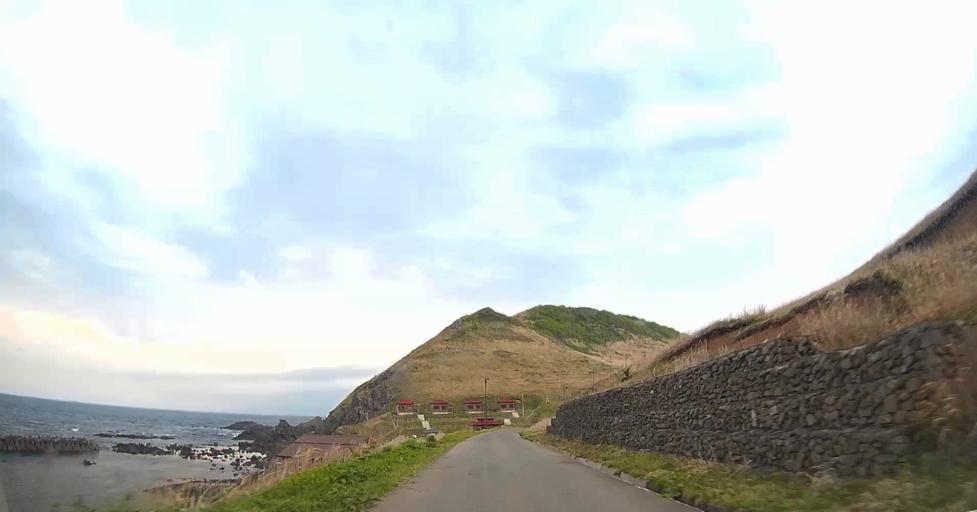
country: JP
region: Aomori
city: Shimokizukuri
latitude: 41.2517
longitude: 140.3432
